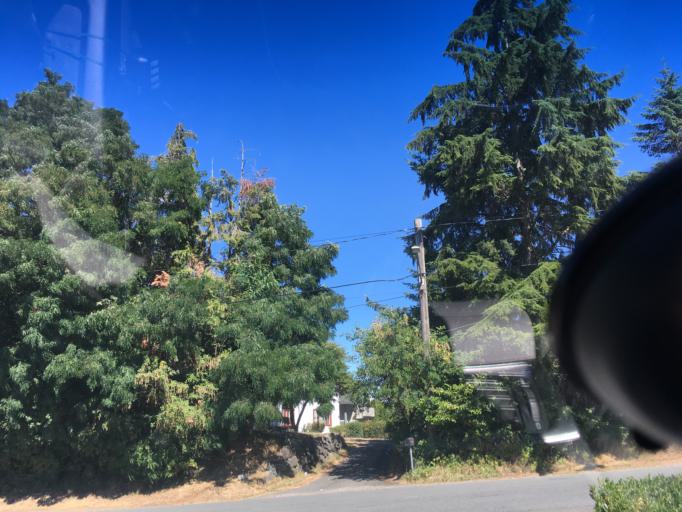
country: US
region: Washington
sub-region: King County
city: Shoreline
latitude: 47.6966
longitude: -122.3716
